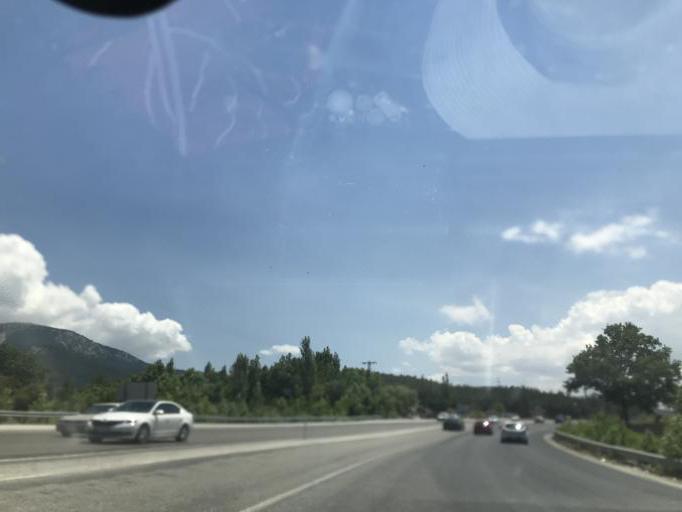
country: TR
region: Denizli
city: Honaz
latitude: 37.6816
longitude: 29.2239
